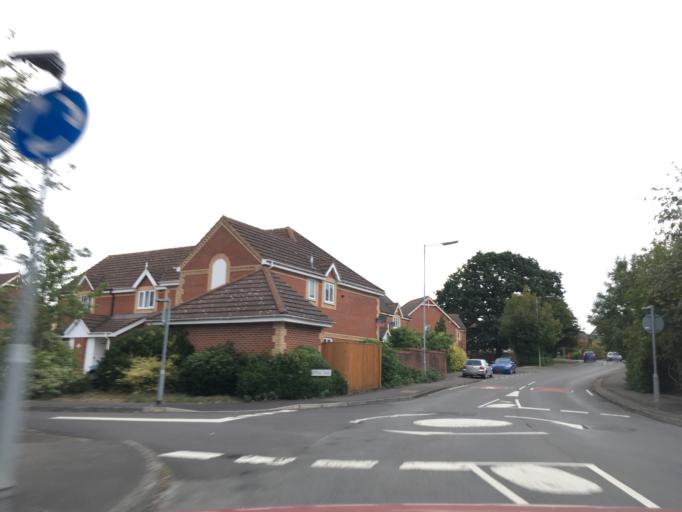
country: GB
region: England
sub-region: Wiltshire
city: Chippenham
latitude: 51.4480
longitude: -2.1108
